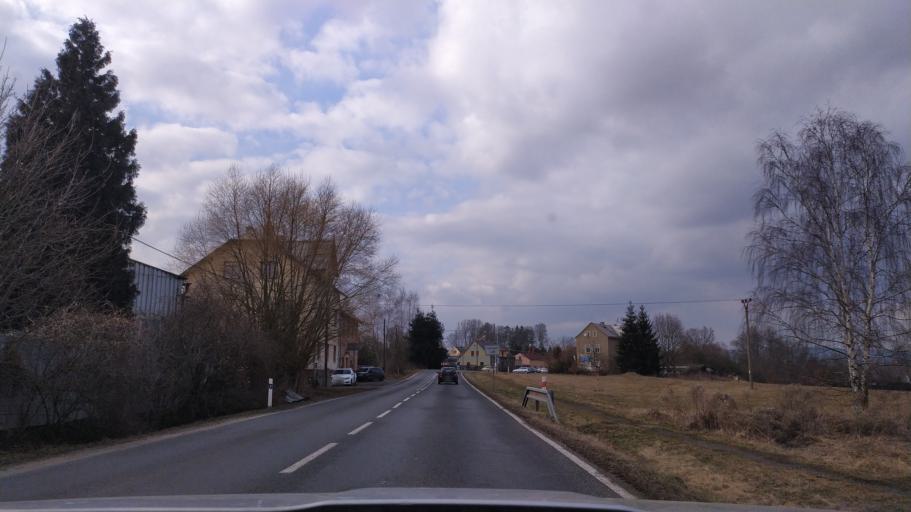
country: CZ
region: Karlovarsky
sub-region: Okres Cheb
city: Frantiskovy Lazne
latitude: 50.1085
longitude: 12.3557
